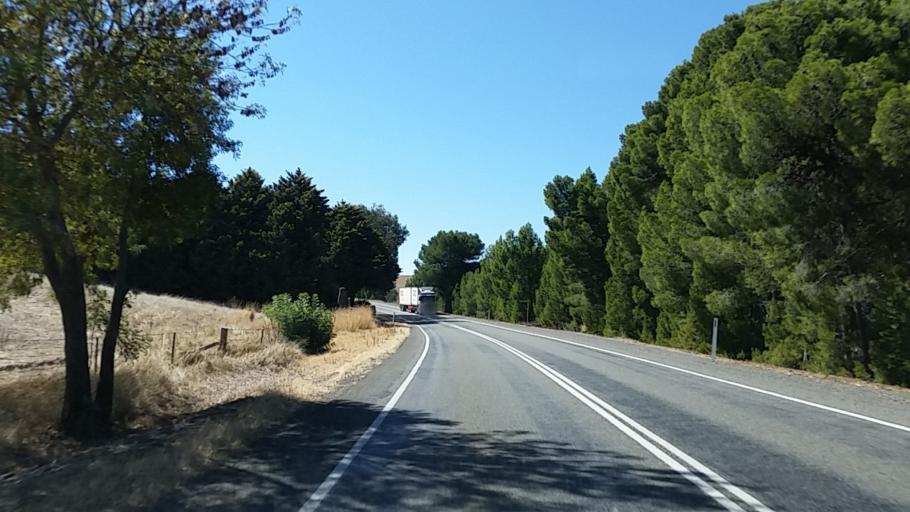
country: AU
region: South Australia
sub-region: Light
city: Kapunda
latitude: -34.0753
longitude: 138.7865
